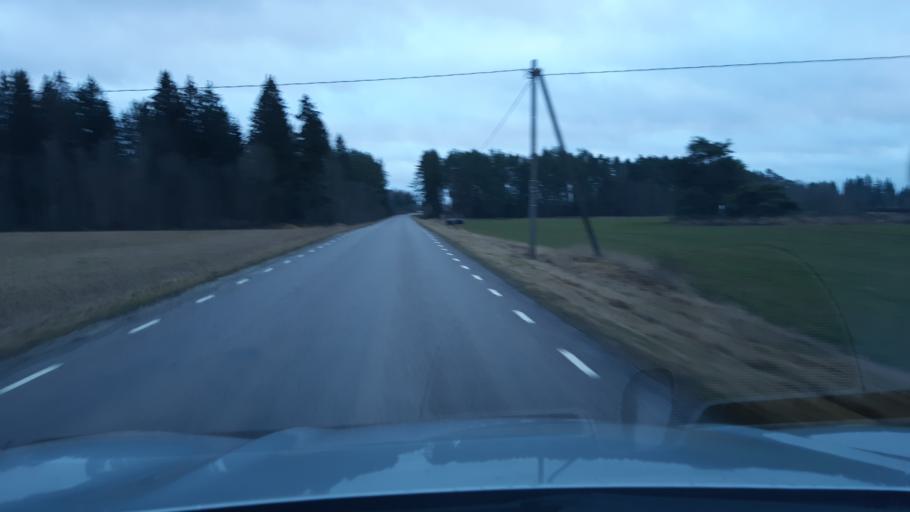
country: EE
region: Raplamaa
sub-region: Kohila vald
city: Kohila
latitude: 59.0758
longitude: 24.6797
